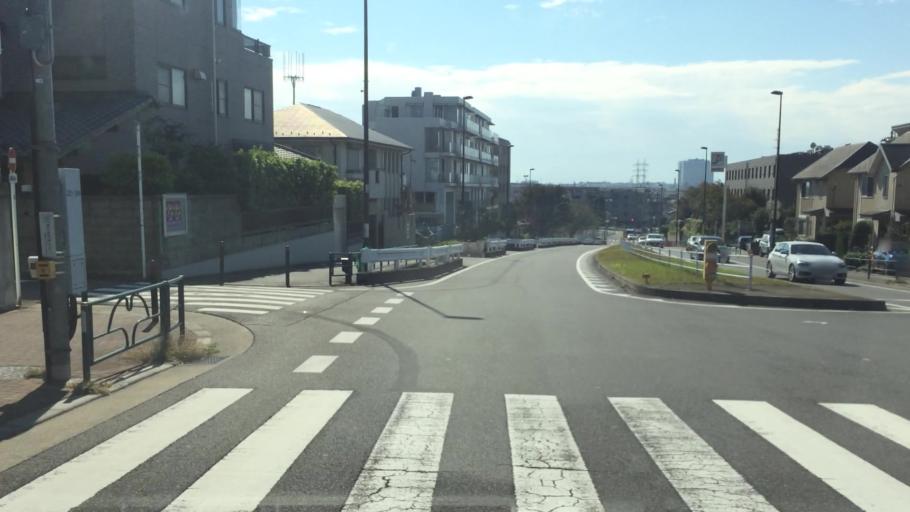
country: JP
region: Tokyo
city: Tokyo
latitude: 35.6022
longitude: 139.6475
